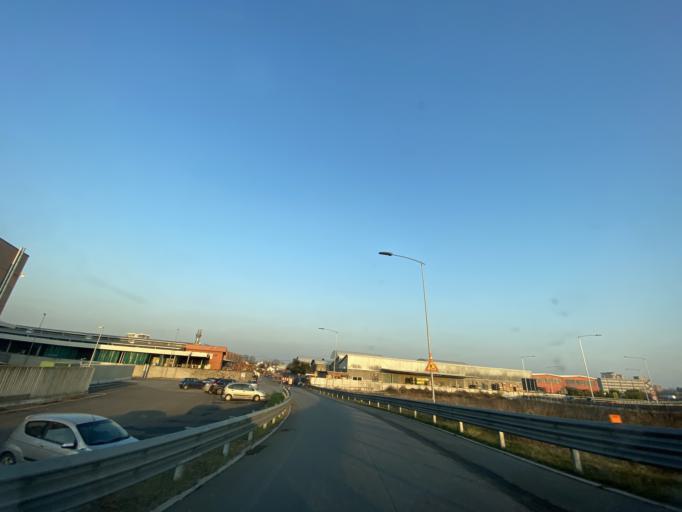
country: IT
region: Lombardy
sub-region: Citta metropolitana di Milano
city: Baranzate
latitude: 45.5314
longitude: 9.1004
